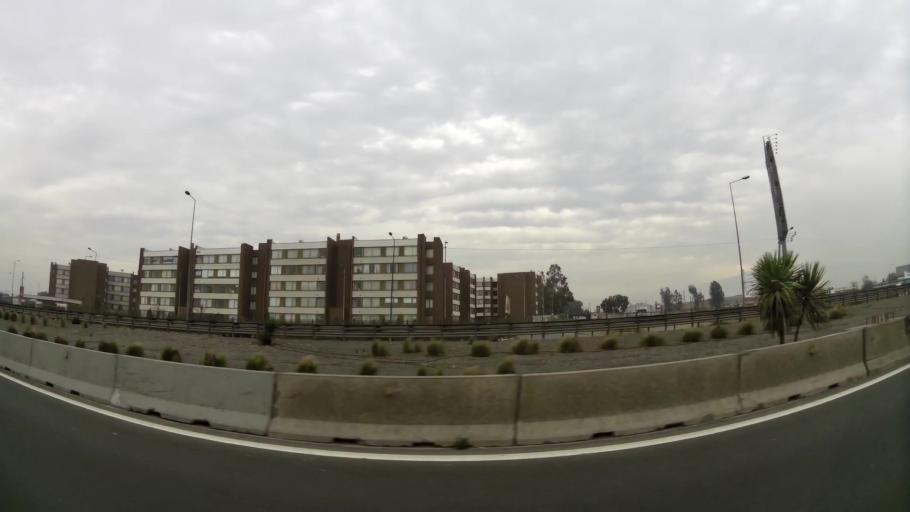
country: CL
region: Santiago Metropolitan
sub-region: Provincia de Santiago
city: Lo Prado
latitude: -33.5088
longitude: -70.7246
